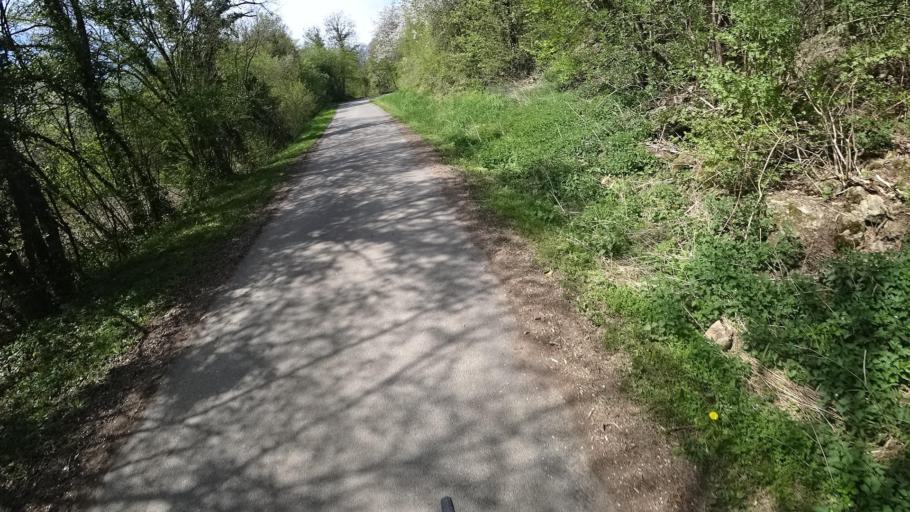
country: DE
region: Rheinland-Pfalz
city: Menningen
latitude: 49.8416
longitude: 6.4794
